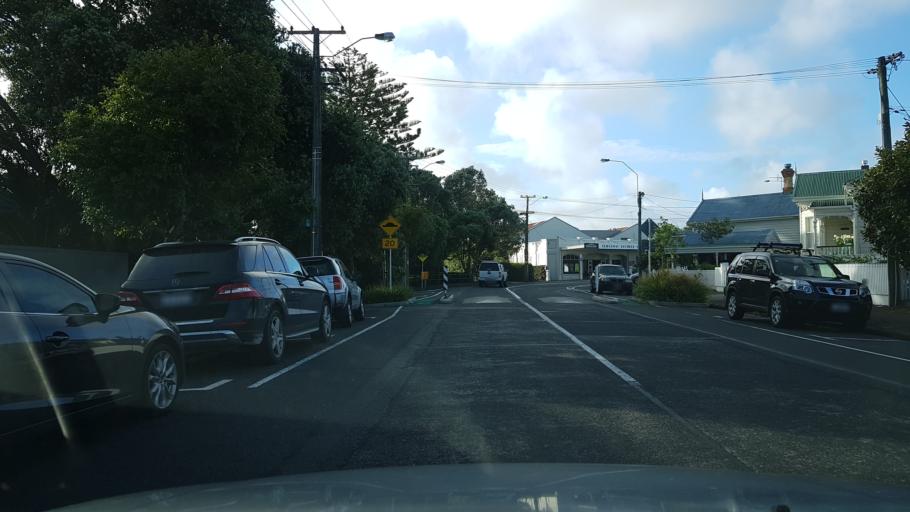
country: NZ
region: Auckland
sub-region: Auckland
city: North Shore
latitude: -36.8187
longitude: 174.7458
